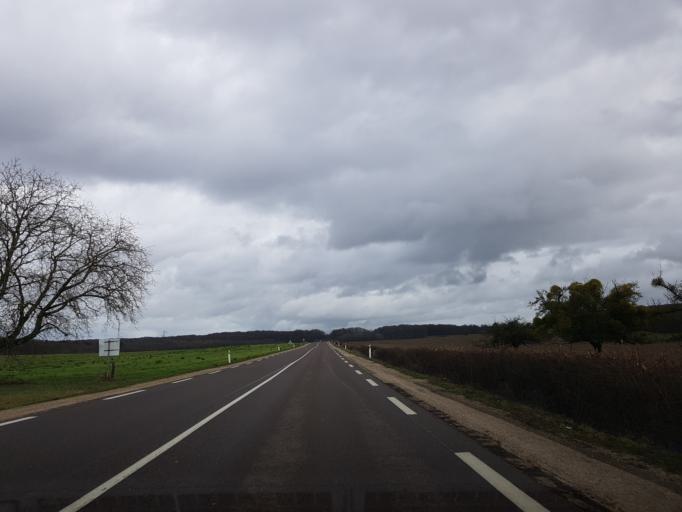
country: FR
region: Franche-Comte
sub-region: Departement de la Haute-Saone
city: Scey-sur-Saone-et-Saint-Albin
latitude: 47.7094
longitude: 5.9086
